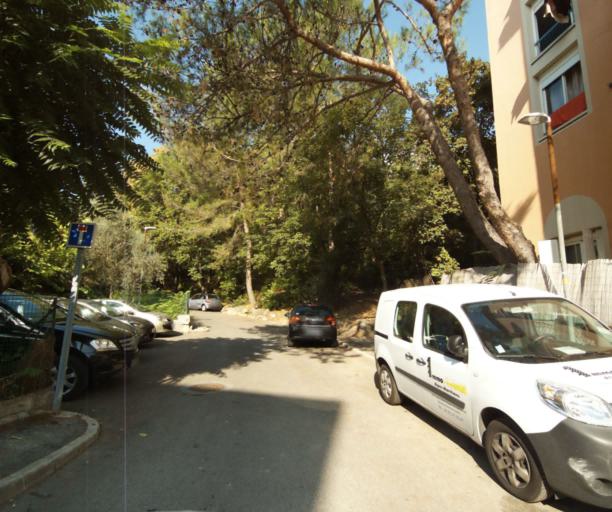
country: FR
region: Provence-Alpes-Cote d'Azur
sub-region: Departement des Alpes-Maritimes
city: Cantaron
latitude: 43.7699
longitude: 7.3293
